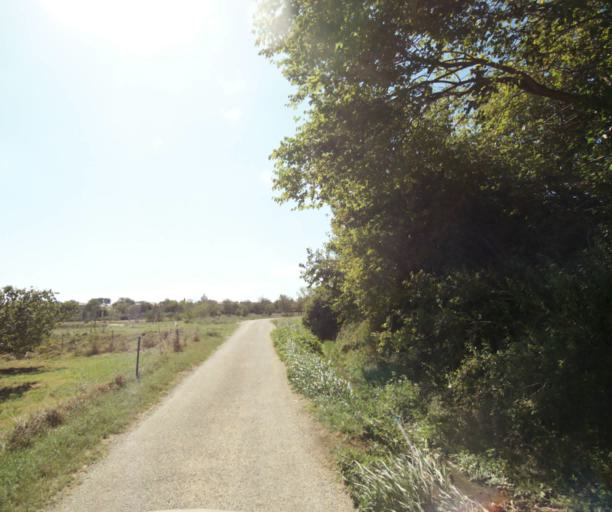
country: FR
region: Languedoc-Roussillon
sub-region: Departement du Gard
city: Bouillargues
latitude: 43.8071
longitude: 4.4256
